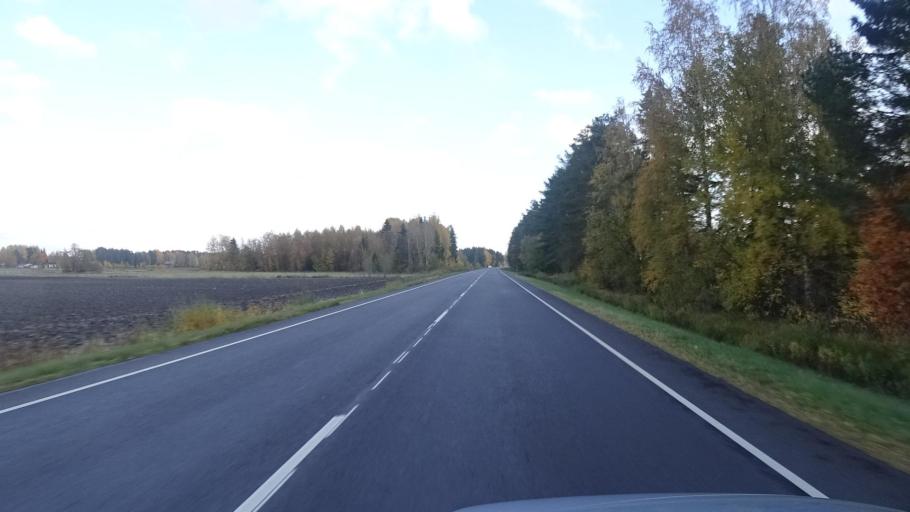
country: FI
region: Satakunta
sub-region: Rauma
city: Koeylioe
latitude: 61.0856
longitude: 22.2611
